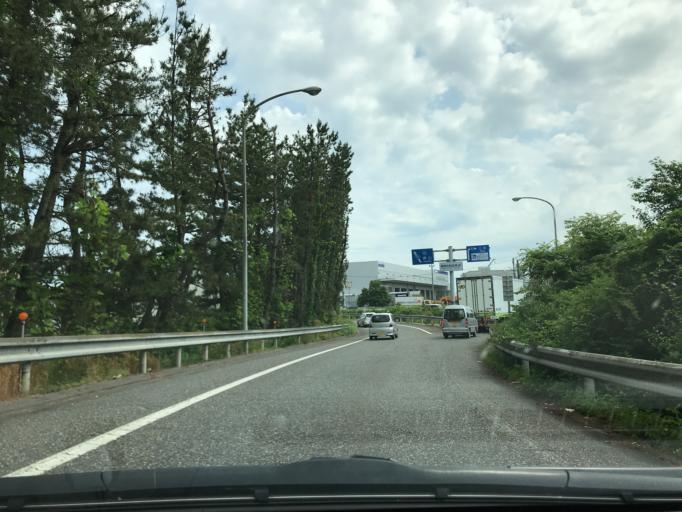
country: JP
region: Niigata
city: Niigata-shi
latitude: 37.8773
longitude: 139.0137
